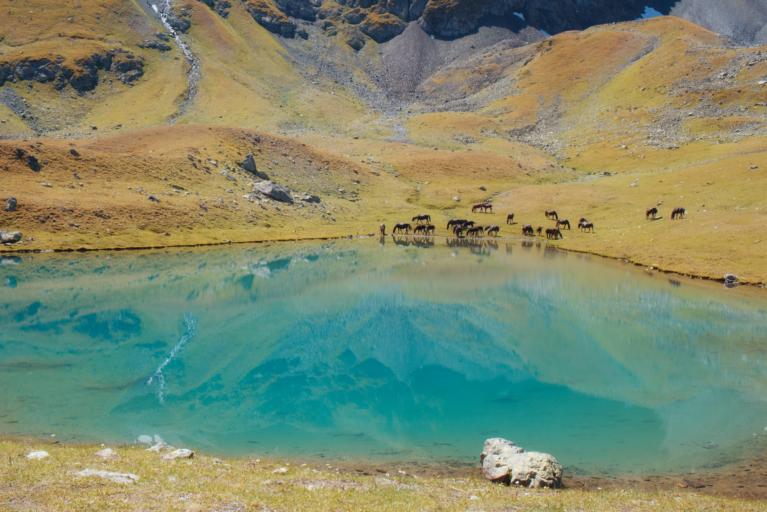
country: RU
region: Karachayevo-Cherkesiya
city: Nizhniy Arkhyz
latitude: 43.6042
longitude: 41.1599
